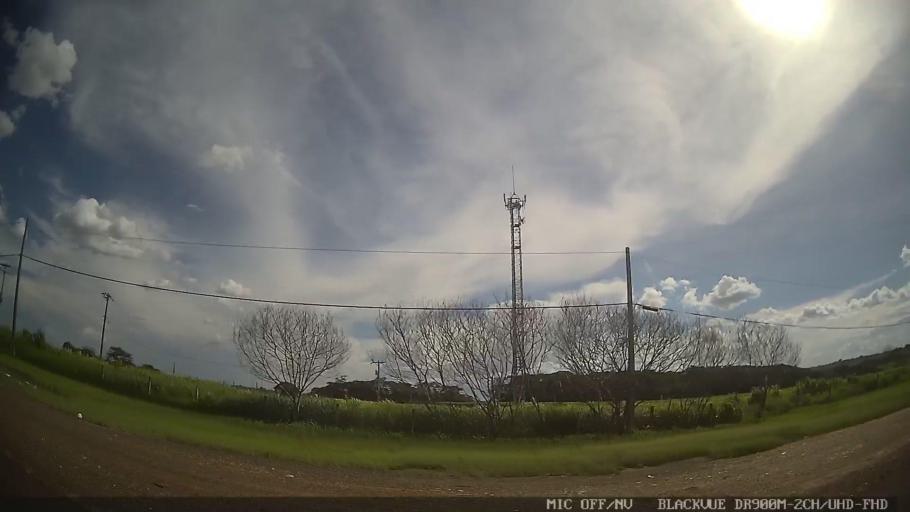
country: BR
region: Sao Paulo
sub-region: Conchas
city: Conchas
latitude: -23.0462
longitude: -47.9574
